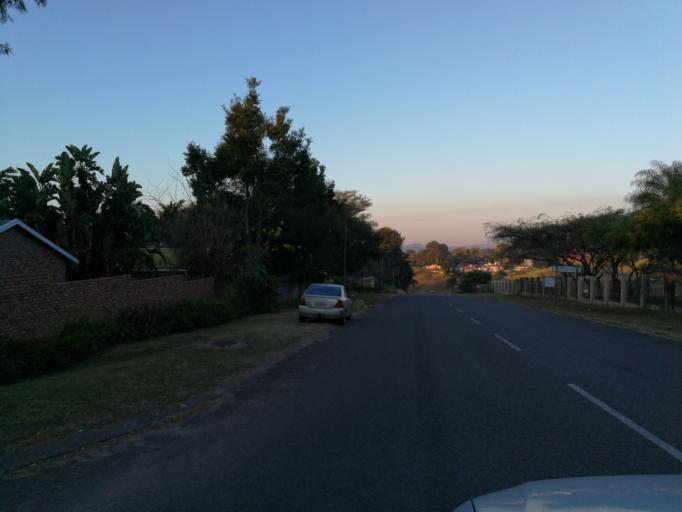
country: ZA
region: Mpumalanga
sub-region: Ehlanzeni District
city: White River
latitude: -25.3192
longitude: 31.0204
